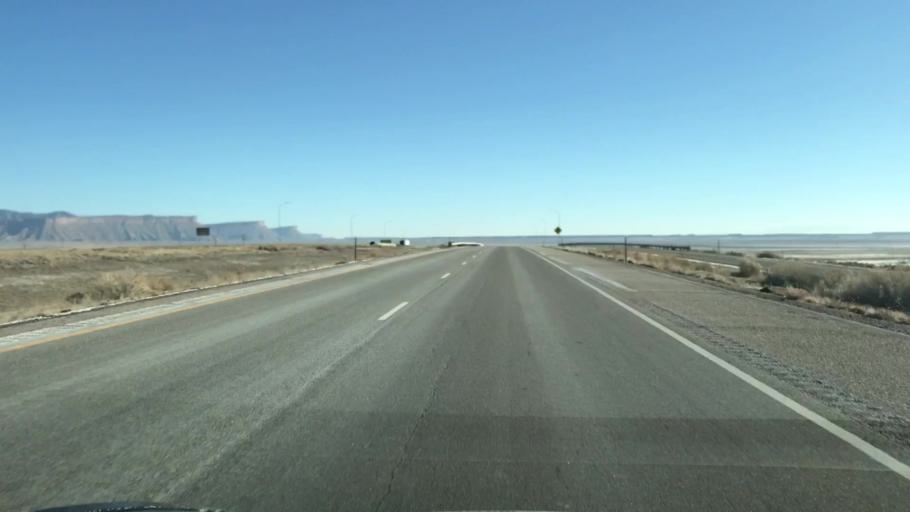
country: US
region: Utah
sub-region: Grand County
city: Moab
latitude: 38.9417
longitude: -109.8142
